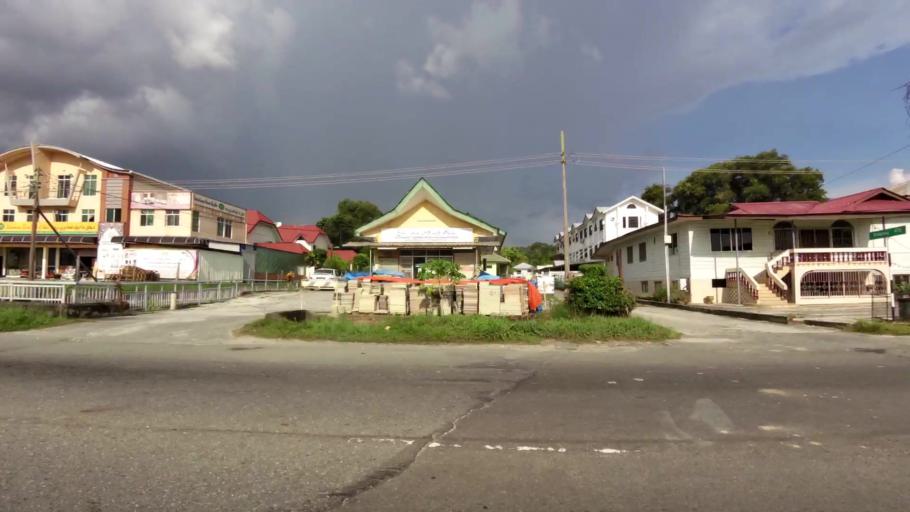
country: BN
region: Brunei and Muara
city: Bandar Seri Begawan
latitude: 4.9631
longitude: 114.9754
